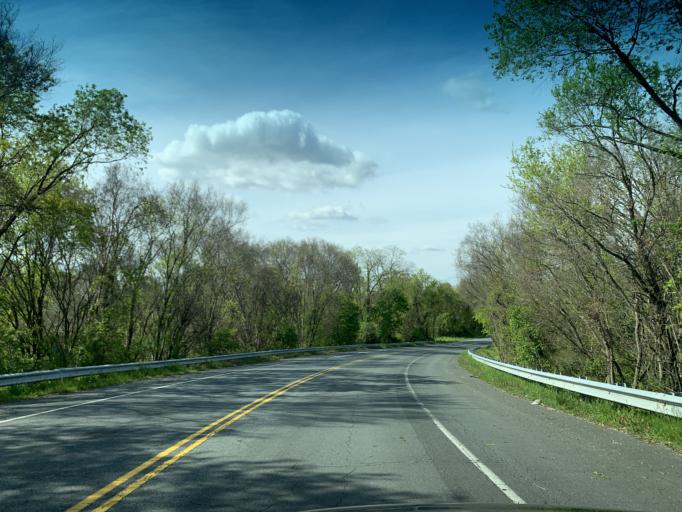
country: US
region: Maryland
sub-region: Harford County
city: Perryman
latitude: 39.4640
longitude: -76.2028
